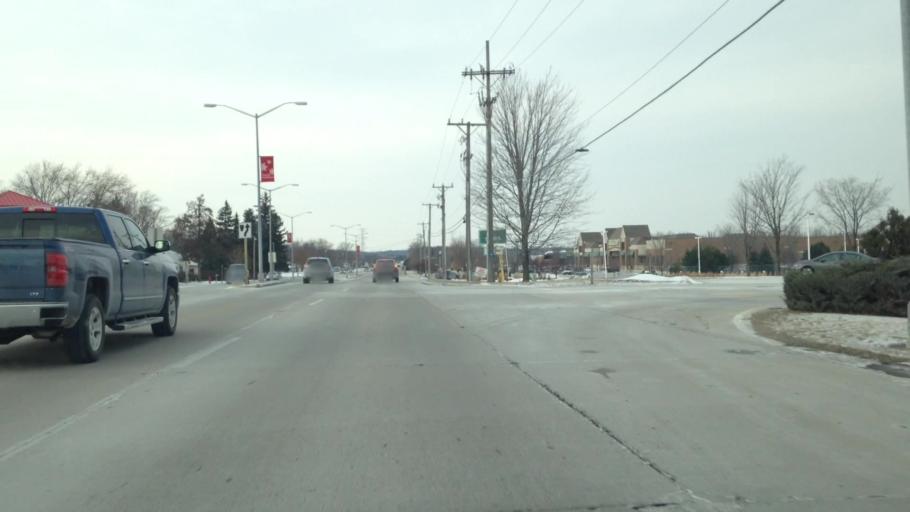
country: US
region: Wisconsin
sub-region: Waukesha County
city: Menomonee Falls
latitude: 43.1928
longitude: -88.1375
